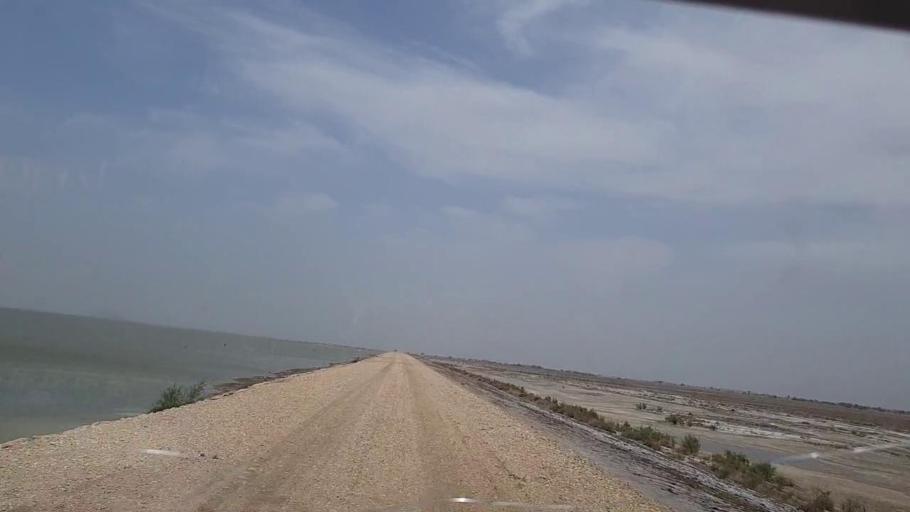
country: PK
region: Sindh
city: Sehwan
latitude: 26.4135
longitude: 67.7744
